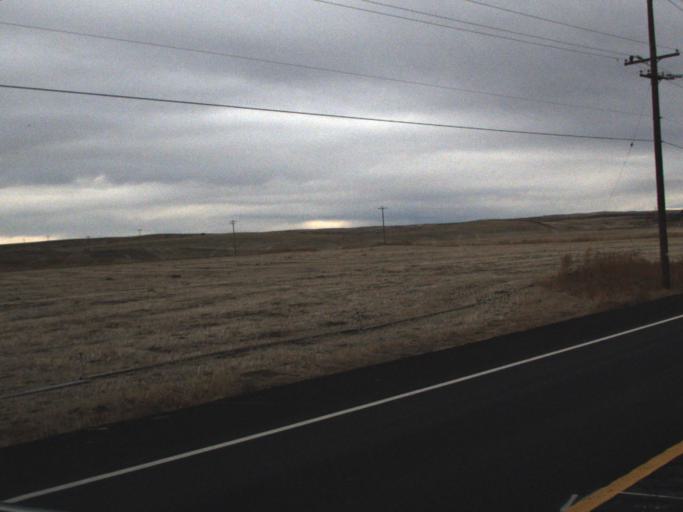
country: US
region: Washington
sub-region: Walla Walla County
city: Garrett
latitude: 46.0440
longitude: -118.6445
